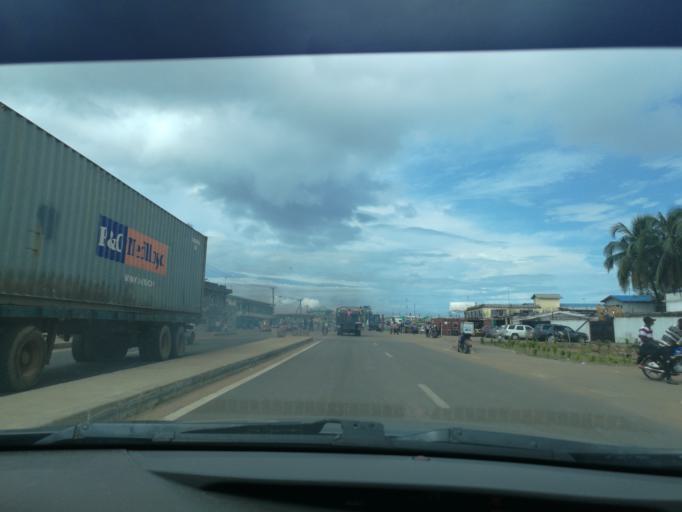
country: LR
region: Montserrado
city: Monrovia
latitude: 6.3381
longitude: -10.7900
